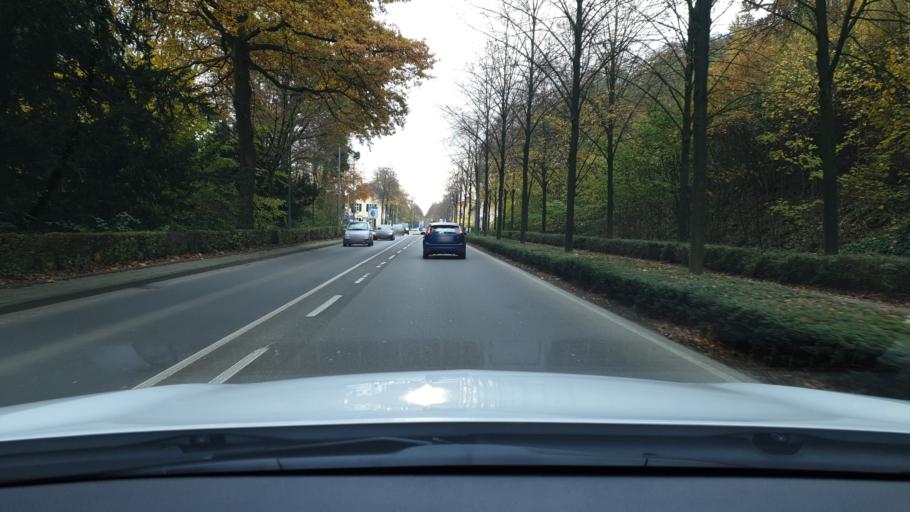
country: DE
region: North Rhine-Westphalia
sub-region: Regierungsbezirk Dusseldorf
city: Kleve
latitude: 51.7950
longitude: 6.1273
